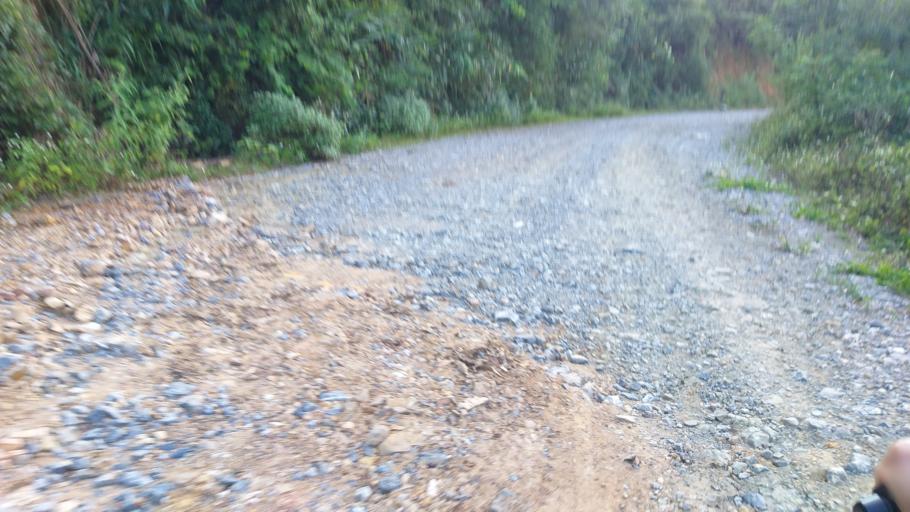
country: LA
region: Phongsali
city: Khoa
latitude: 21.2167
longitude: 102.5930
